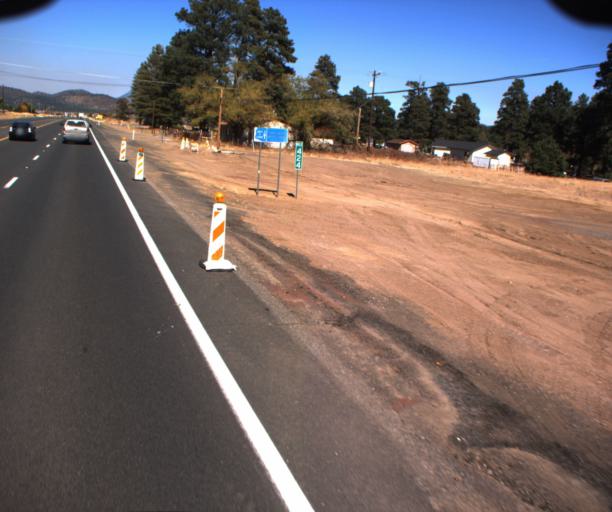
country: US
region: Arizona
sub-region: Coconino County
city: Flagstaff
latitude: 35.2870
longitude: -111.5422
